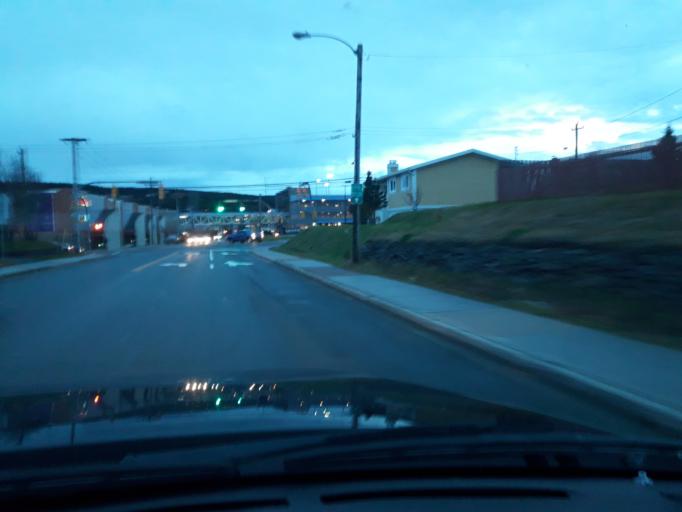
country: CA
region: Newfoundland and Labrador
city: St. John's
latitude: 47.5632
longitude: -52.7552
